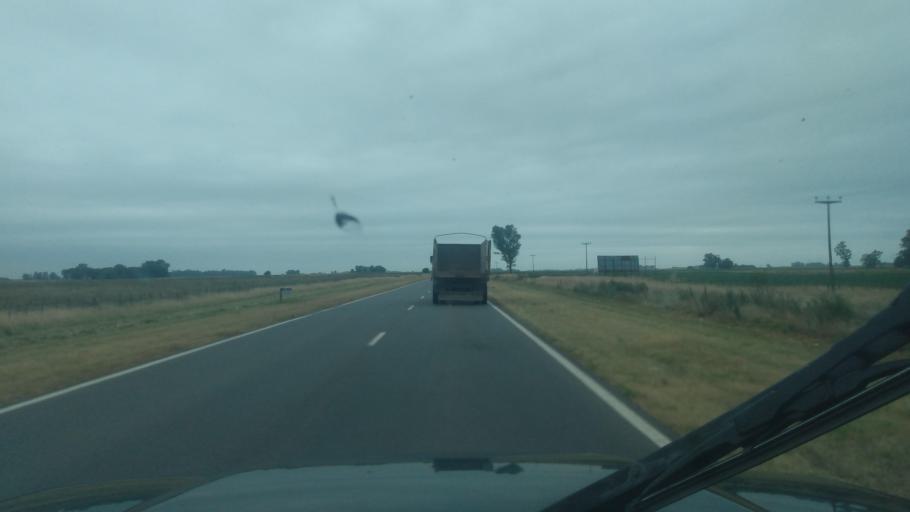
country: AR
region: Buenos Aires
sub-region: Partido de Nueve de Julio
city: Nueve de Julio
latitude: -35.3930
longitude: -60.7404
